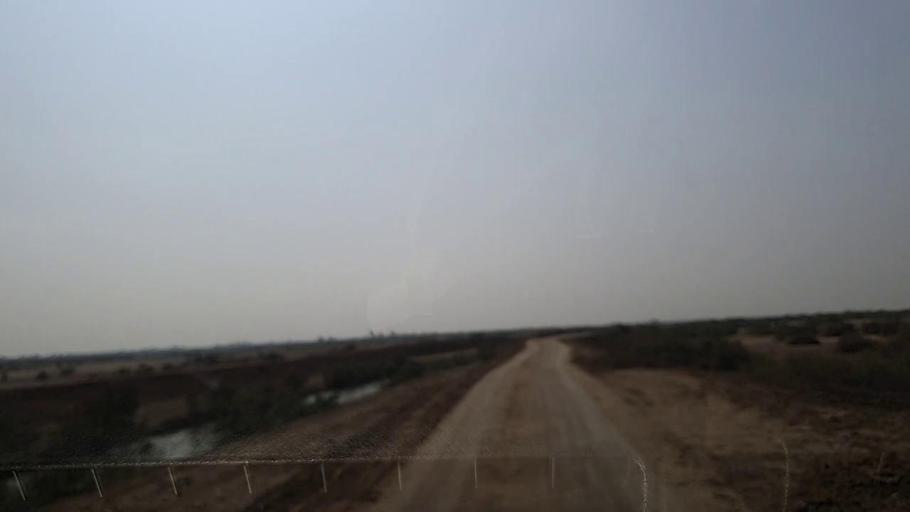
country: PK
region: Sindh
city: Gharo
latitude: 24.6757
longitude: 67.7315
